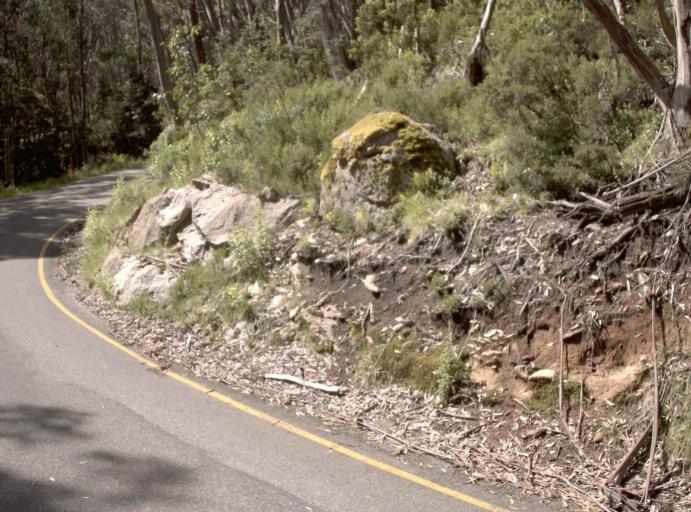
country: AU
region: Victoria
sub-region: Latrobe
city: Moe
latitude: -37.8402
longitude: 146.2510
